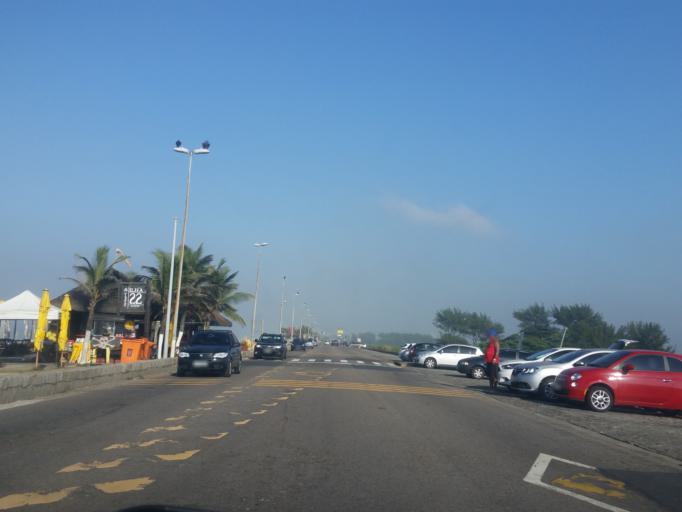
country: BR
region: Rio de Janeiro
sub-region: Rio De Janeiro
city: Rio de Janeiro
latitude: -23.0120
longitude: -43.3820
